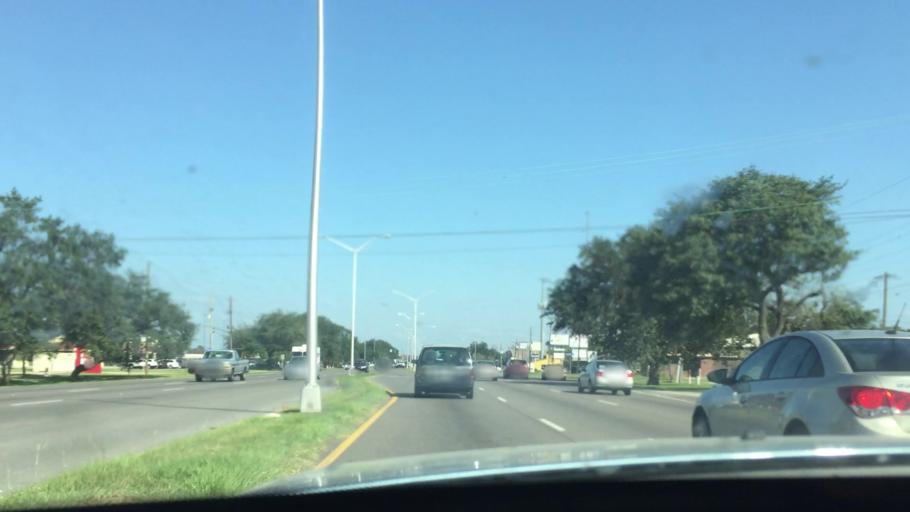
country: US
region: Louisiana
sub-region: East Baton Rouge Parish
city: Baton Rouge
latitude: 30.4515
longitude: -91.1179
